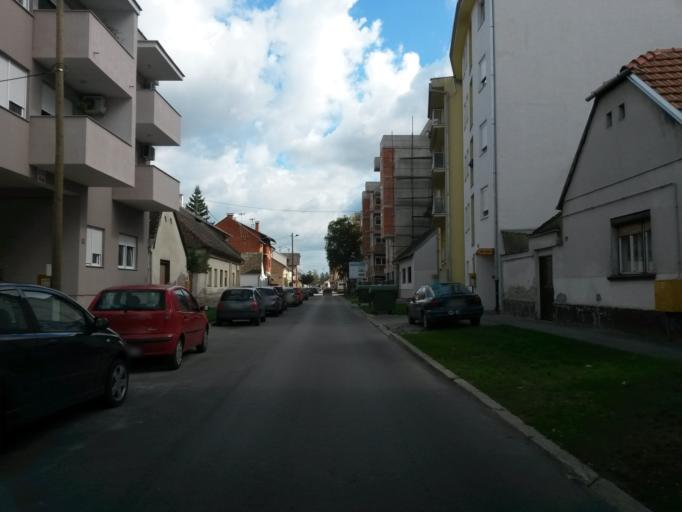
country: HR
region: Osjecko-Baranjska
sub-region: Grad Osijek
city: Osijek
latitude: 45.5590
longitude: 18.6680
